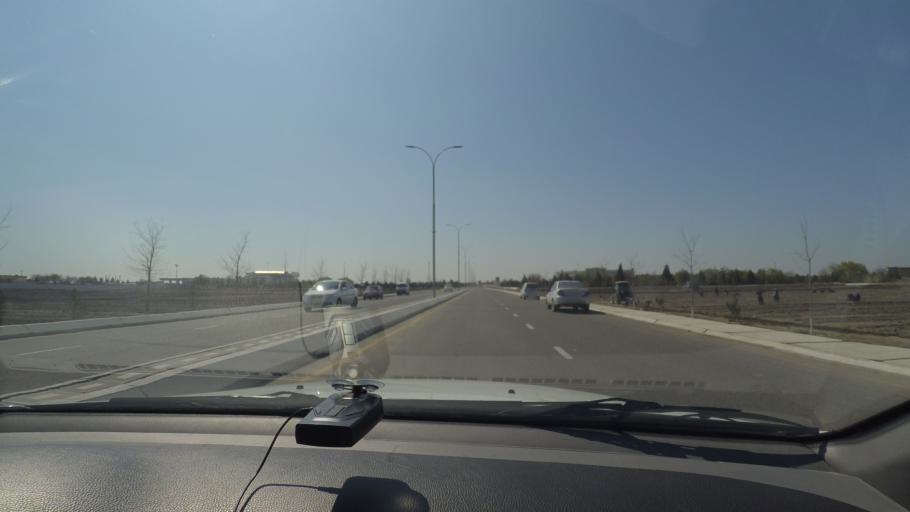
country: UZ
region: Bukhara
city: Bukhara
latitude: 39.7712
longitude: 64.4740
